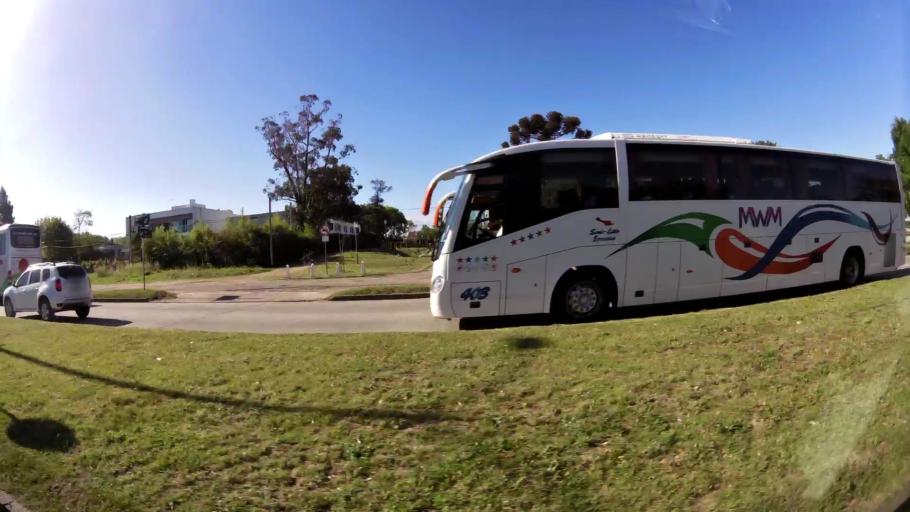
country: UY
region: Canelones
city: Paso de Carrasco
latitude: -34.8779
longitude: -56.0643
